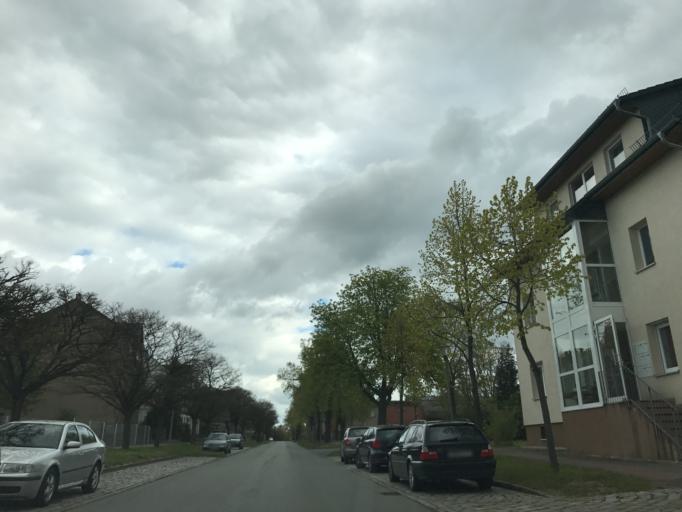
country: DE
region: Brandenburg
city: Wustermark
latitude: 52.5453
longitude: 12.9455
